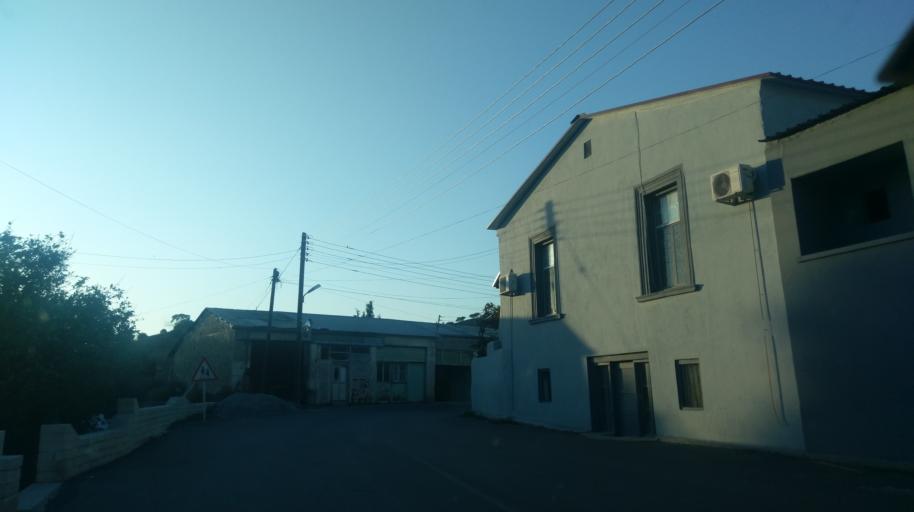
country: CY
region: Lefkosia
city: Nicosia
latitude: 35.2591
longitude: 33.4857
